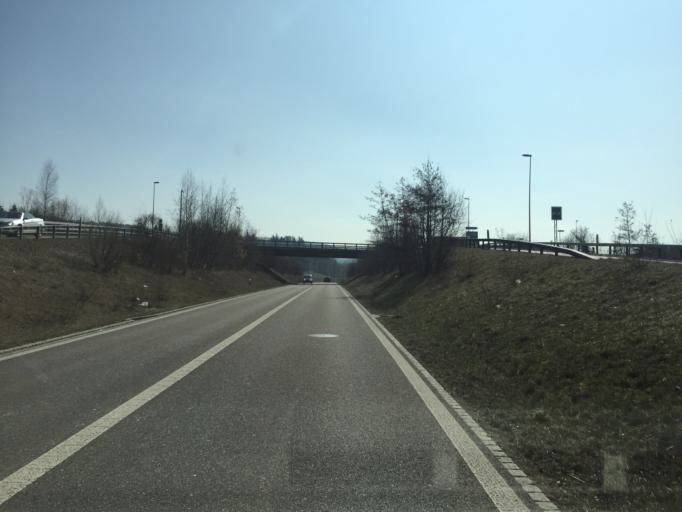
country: CH
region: Saint Gallen
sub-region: Wahlkreis Wil
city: Jonschwil
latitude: 47.4235
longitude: 9.0689
